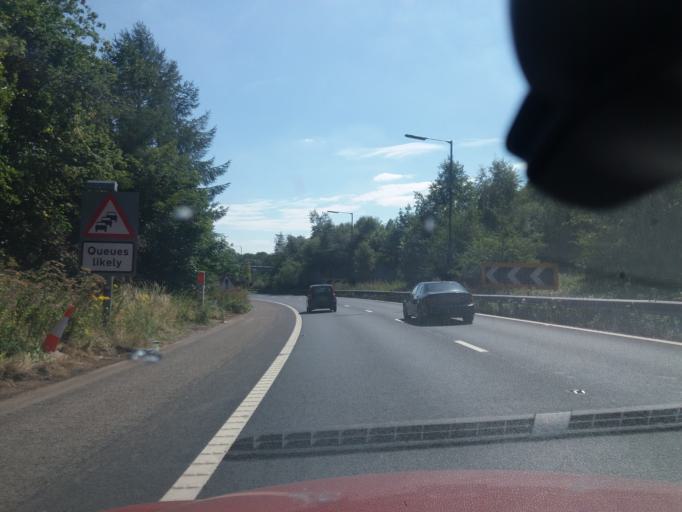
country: GB
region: England
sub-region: Borough of Bolton
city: Kearsley
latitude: 53.5158
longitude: -2.3712
